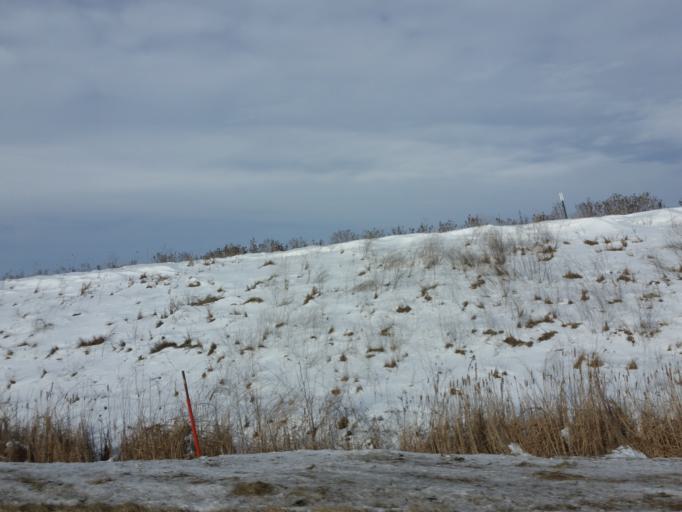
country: US
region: Iowa
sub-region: Buchanan County
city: Independence
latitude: 42.4616
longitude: -91.7371
